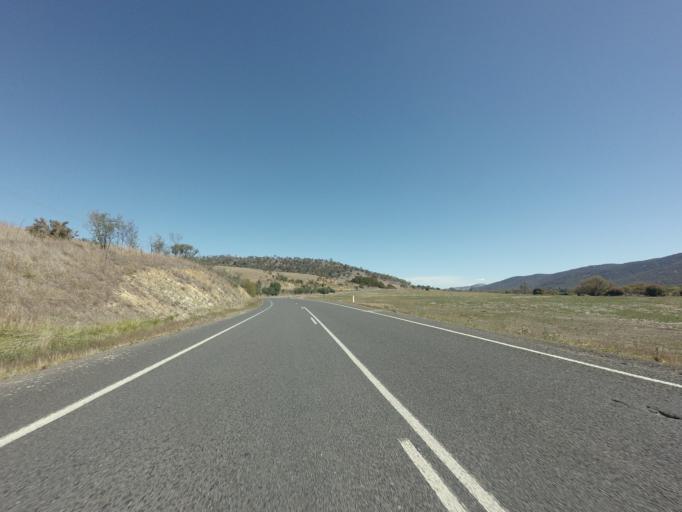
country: AU
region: Tasmania
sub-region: Break O'Day
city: St Helens
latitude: -41.7322
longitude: 147.8197
